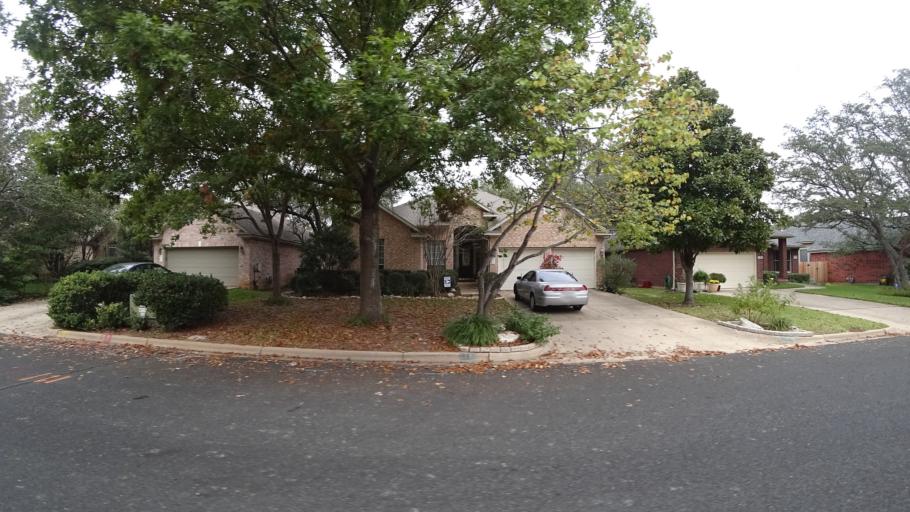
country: US
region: Texas
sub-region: Travis County
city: Shady Hollow
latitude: 30.2149
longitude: -97.8783
